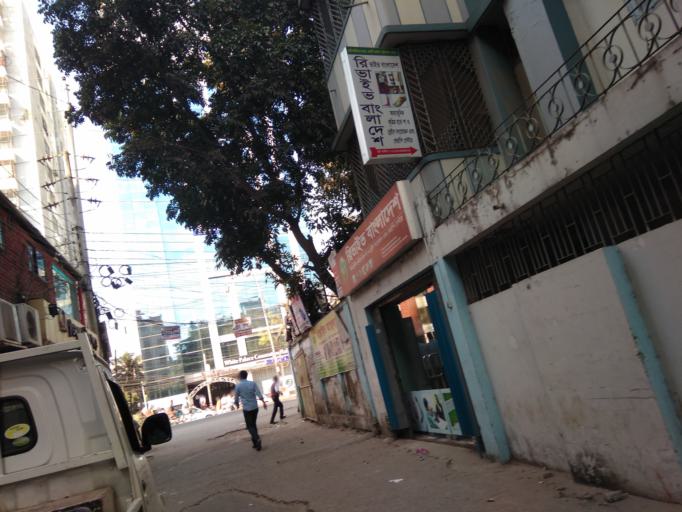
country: BD
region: Dhaka
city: Azimpur
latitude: 23.7737
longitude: 90.3628
